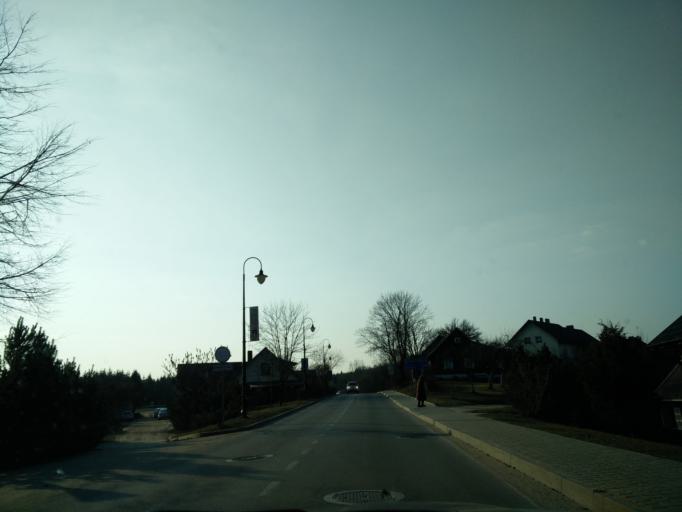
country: LT
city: Trakai
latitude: 54.6527
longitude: 24.9201
